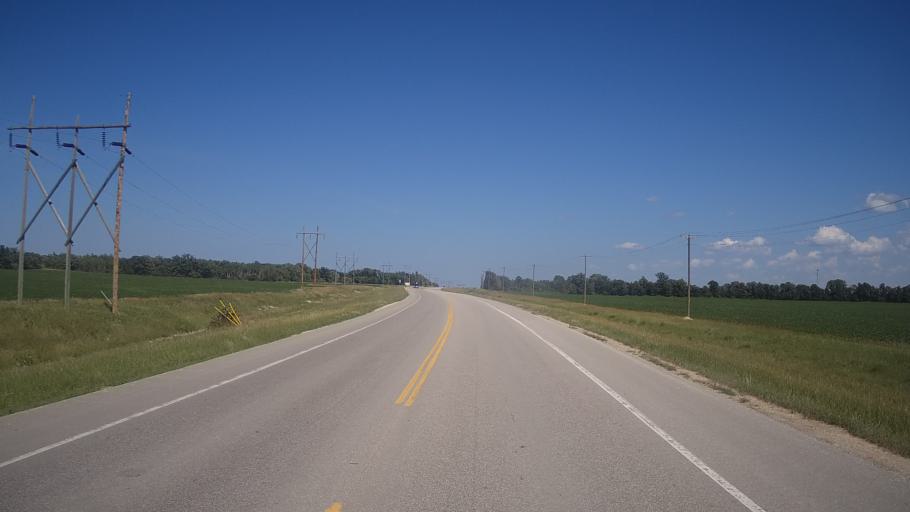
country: CA
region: Manitoba
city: Stonewall
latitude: 50.1228
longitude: -97.3431
